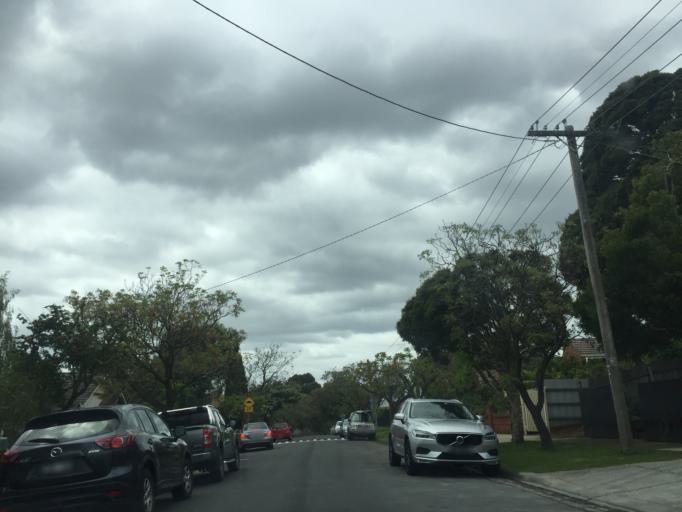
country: AU
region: Victoria
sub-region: Boroondara
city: Kew
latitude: -37.7986
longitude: 145.0408
